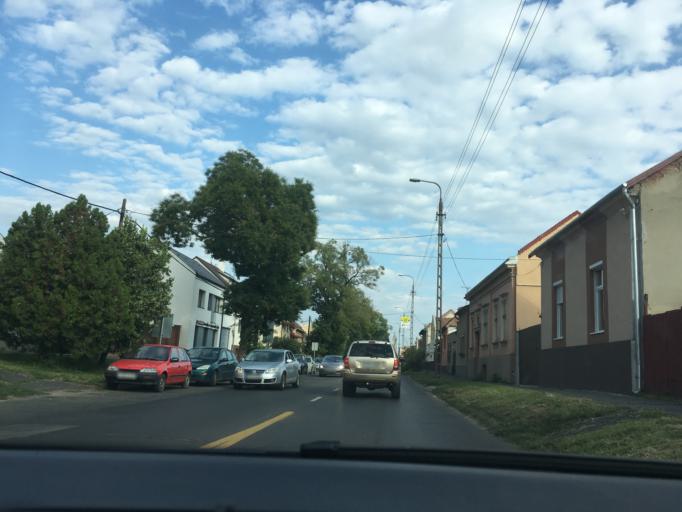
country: HU
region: Hajdu-Bihar
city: Debrecen
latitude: 47.5413
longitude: 21.6285
